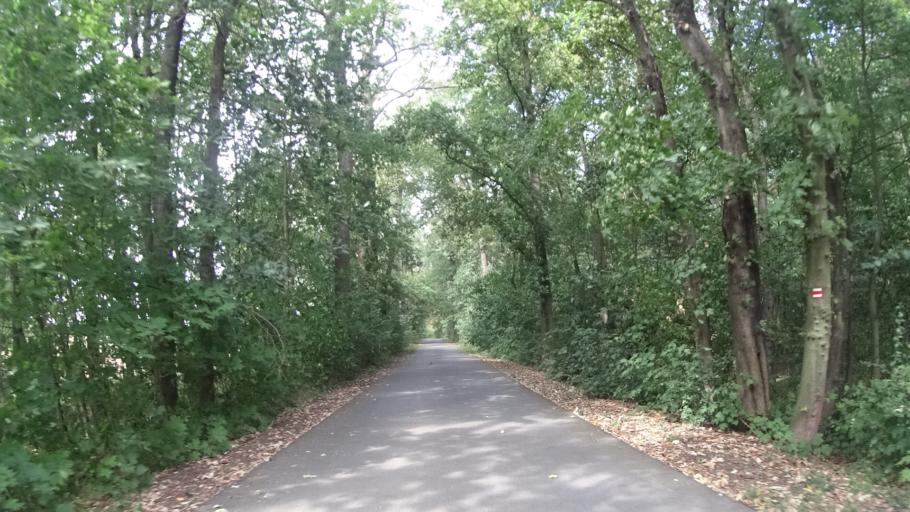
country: CZ
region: Olomoucky
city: Horka nad Moravou
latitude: 49.6457
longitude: 17.1970
